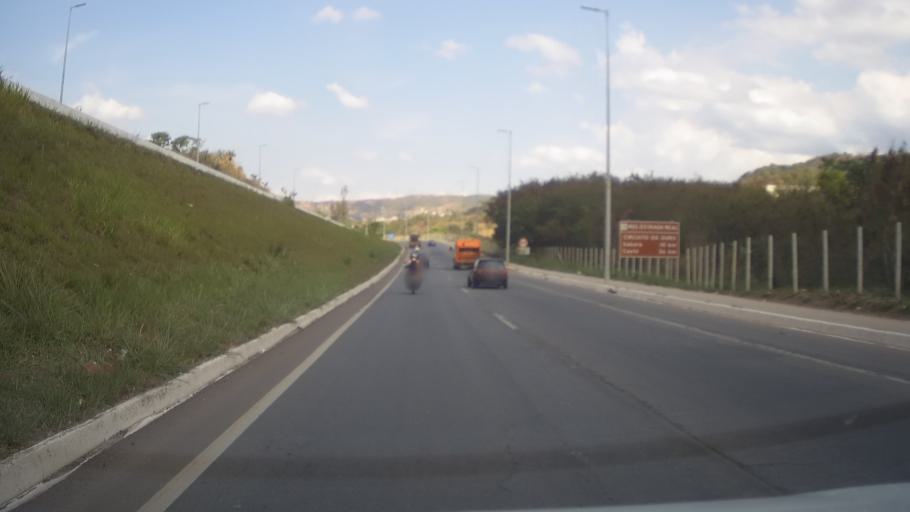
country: BR
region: Minas Gerais
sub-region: Belo Horizonte
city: Belo Horizonte
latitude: -19.8730
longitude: -43.8818
